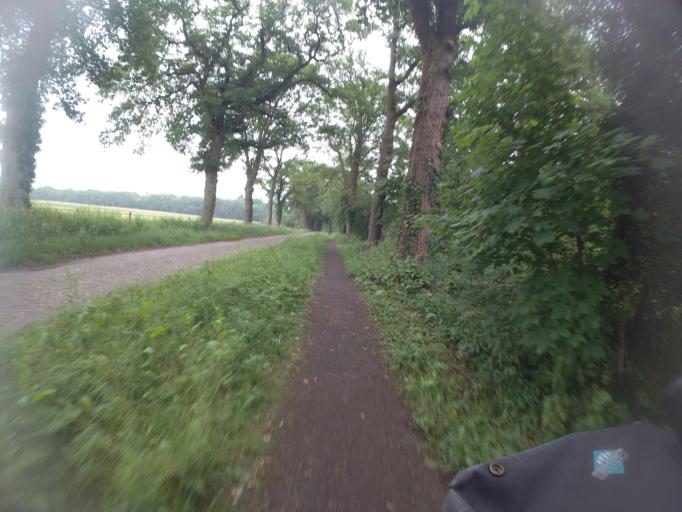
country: NL
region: Drenthe
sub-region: Gemeente Westerveld
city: Dwingeloo
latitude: 52.8173
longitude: 6.3442
